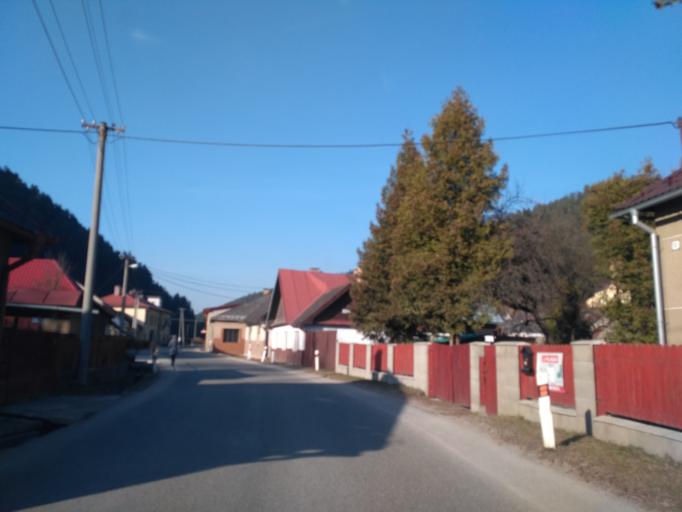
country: SK
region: Kosicky
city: Medzev
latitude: 48.7449
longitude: 20.7737
